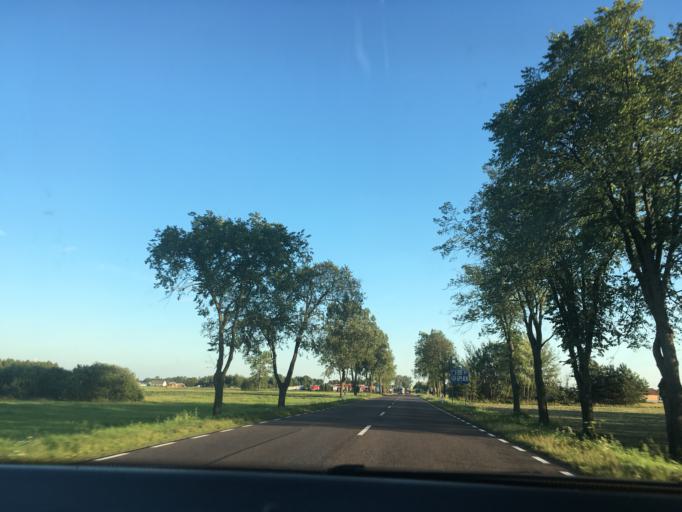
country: PL
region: Lublin Voivodeship
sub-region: Powiat bialski
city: Rzeczyca
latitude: 51.9113
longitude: 22.7066
